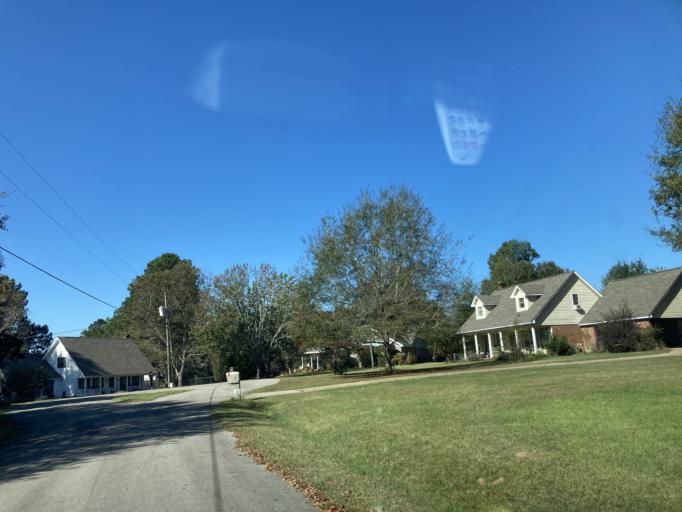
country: US
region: Mississippi
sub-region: Lamar County
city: West Hattiesburg
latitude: 31.2986
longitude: -89.4057
